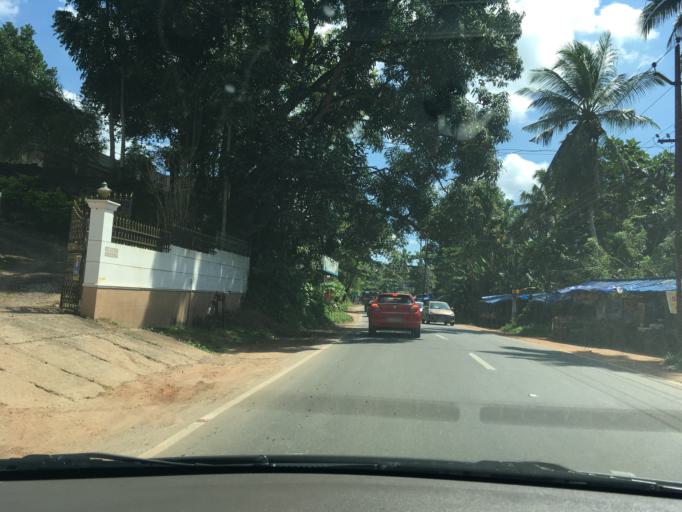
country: IN
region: Kerala
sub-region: Thiruvananthapuram
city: Nedumangad
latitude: 8.5918
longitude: 76.9952
